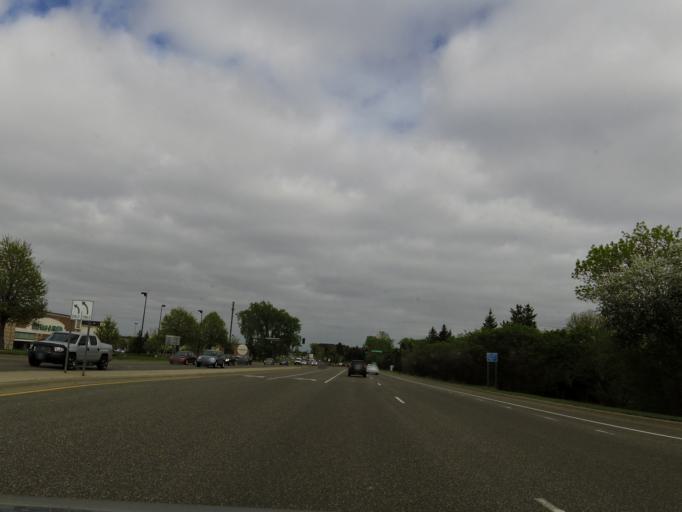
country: US
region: Minnesota
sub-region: Washington County
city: Woodbury
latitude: 44.9249
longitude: -92.9645
